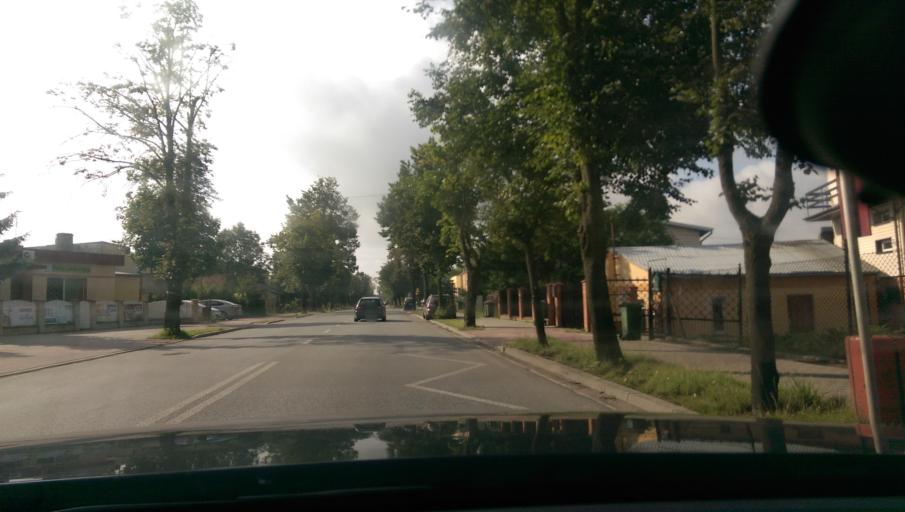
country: PL
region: Masovian Voivodeship
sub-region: Powiat ciechanowski
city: Ciechanow
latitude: 52.8658
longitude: 20.6266
